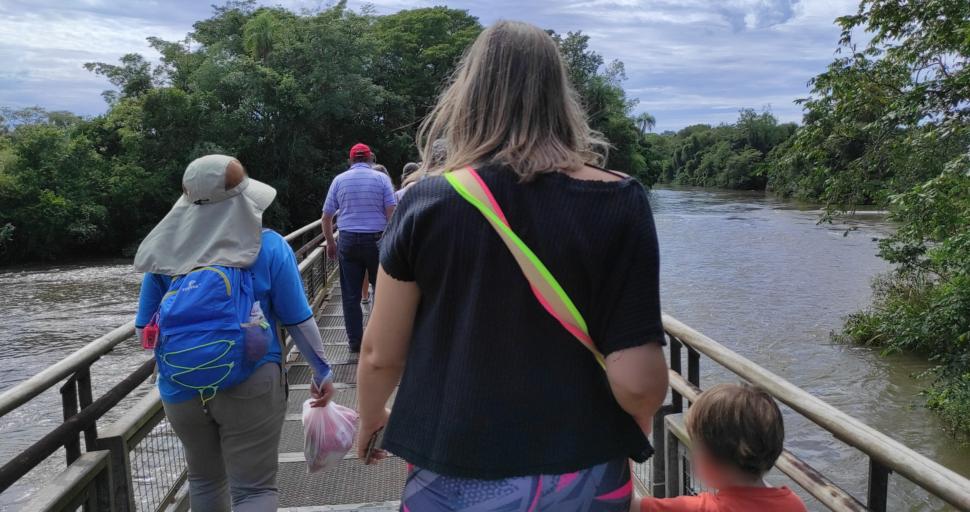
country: AR
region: Misiones
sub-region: Departamento de Iguazu
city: Puerto Iguazu
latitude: -25.7005
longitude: -54.4441
